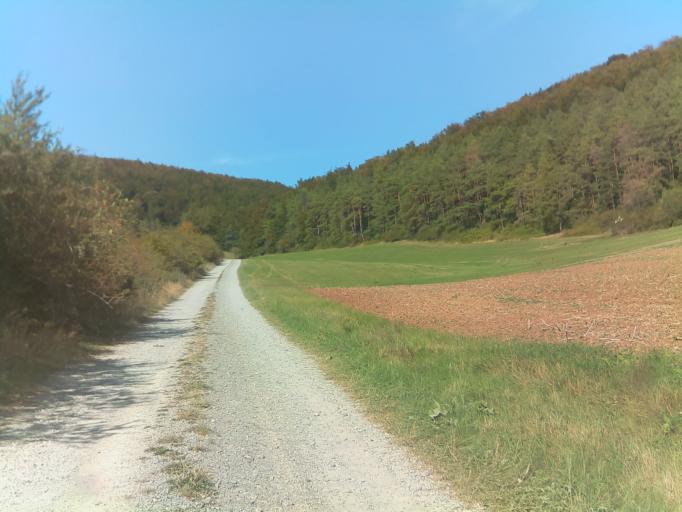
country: DE
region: Thuringia
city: Henneberg
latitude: 50.5256
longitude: 10.3276
